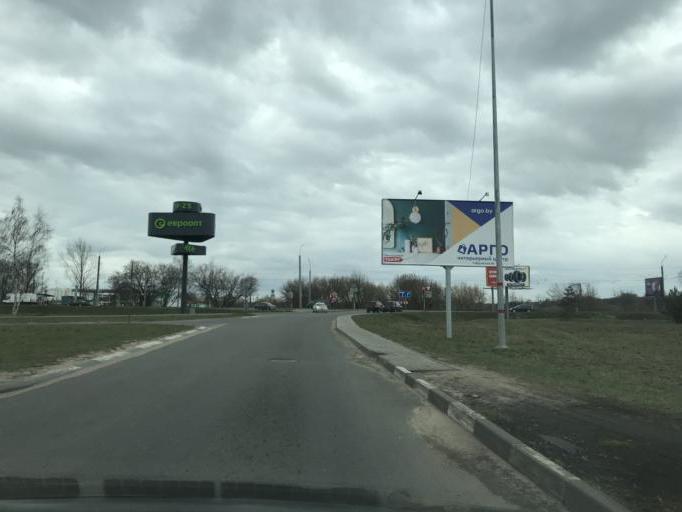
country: BY
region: Mogilev
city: Mahilyow
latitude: 53.8806
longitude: 30.3146
